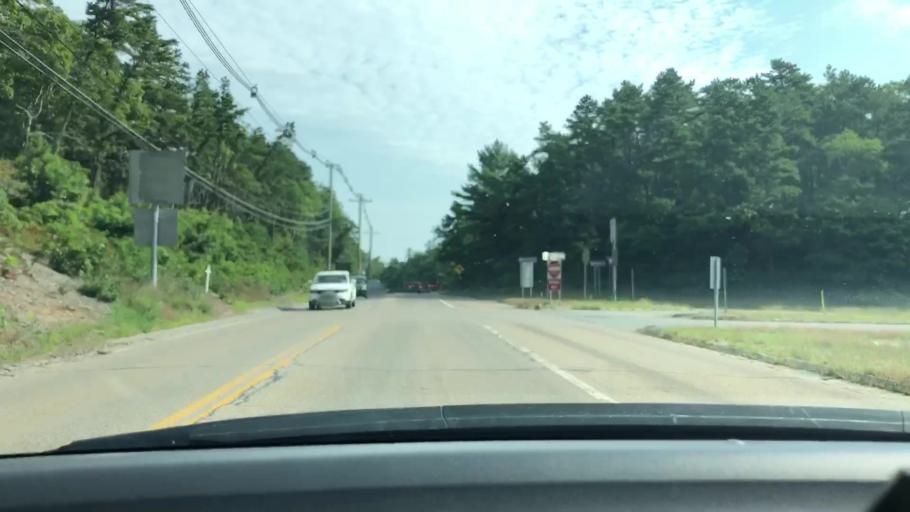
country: US
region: Massachusetts
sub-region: Plymouth County
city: White Island Shores
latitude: 41.8746
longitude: -70.6002
